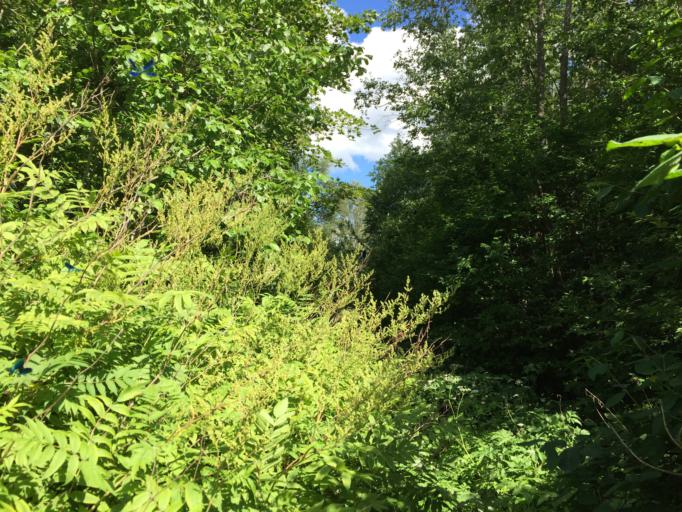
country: LT
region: Panevezys
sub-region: Birzai
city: Birzai
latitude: 56.3754
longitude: 24.6349
